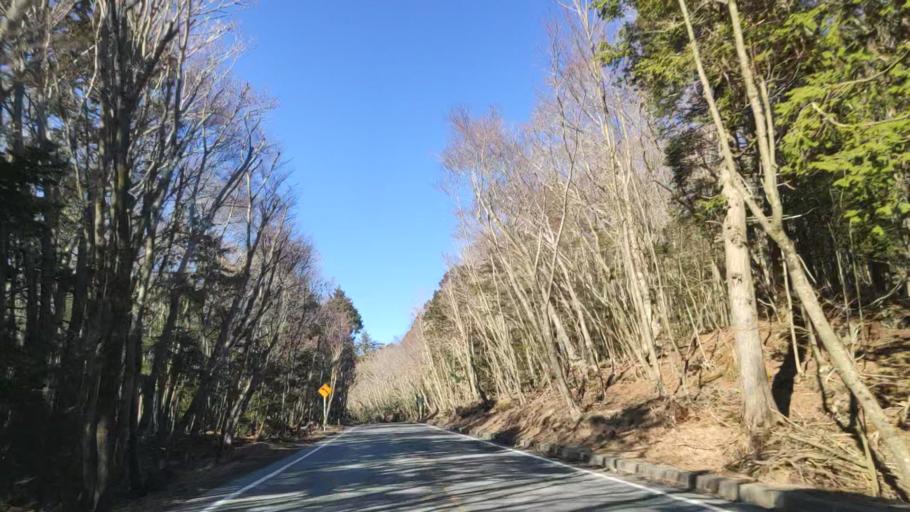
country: JP
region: Yamanashi
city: Fujikawaguchiko
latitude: 35.4475
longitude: 138.6412
